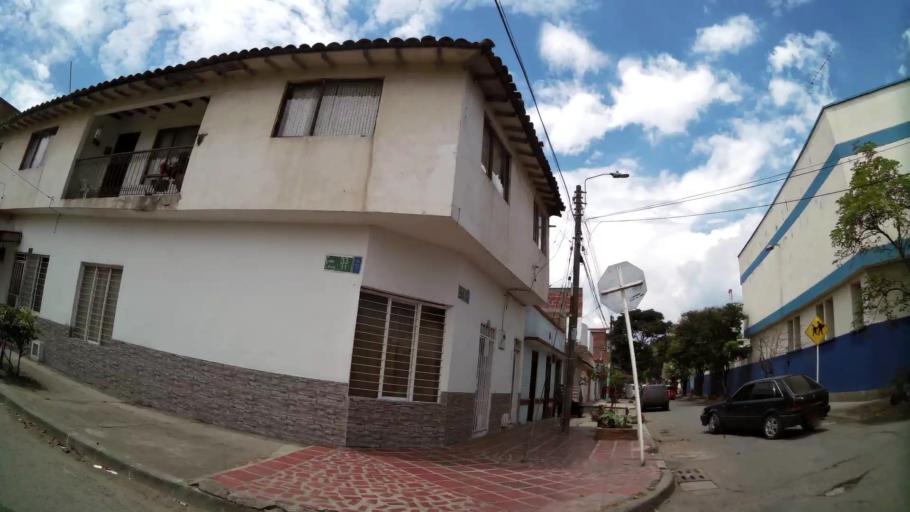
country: CO
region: Valle del Cauca
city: Cali
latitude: 3.4472
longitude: -76.5107
